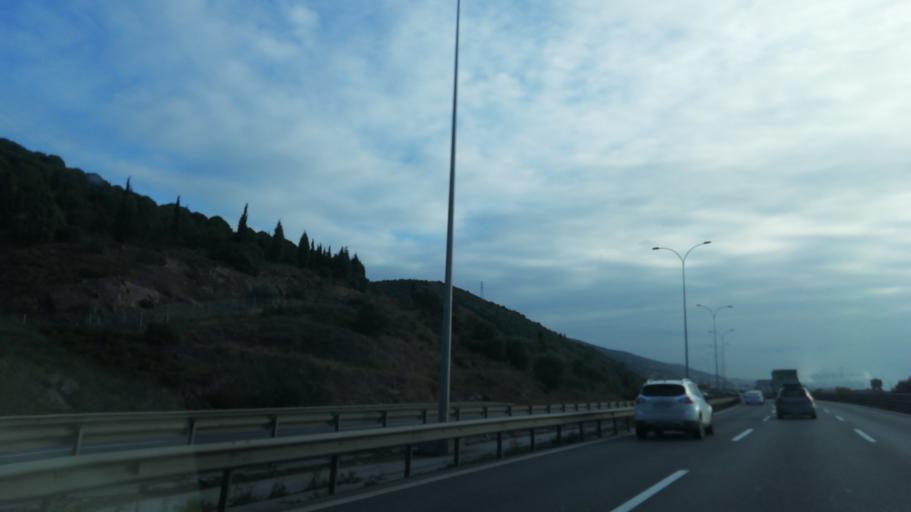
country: TR
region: Kocaeli
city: Hereke
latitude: 40.7789
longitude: 29.6752
